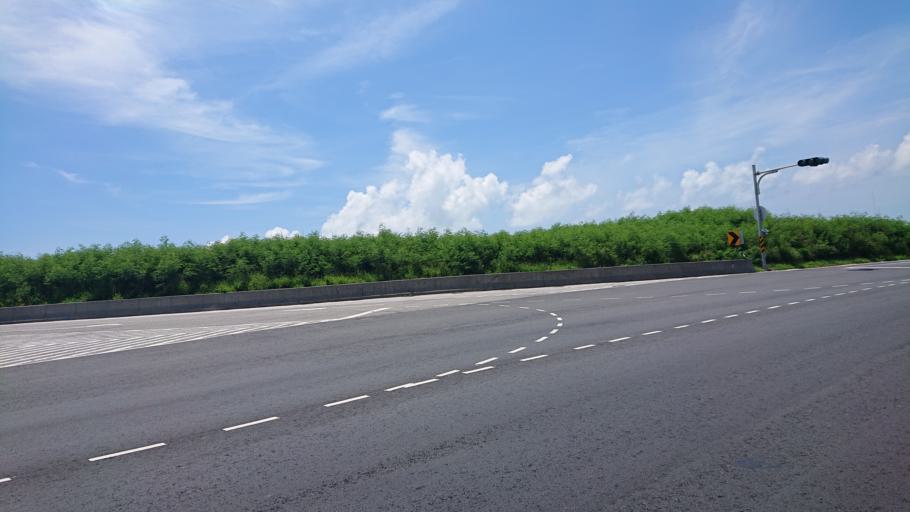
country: TW
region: Taiwan
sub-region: Penghu
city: Ma-kung
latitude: 23.6179
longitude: 119.6059
